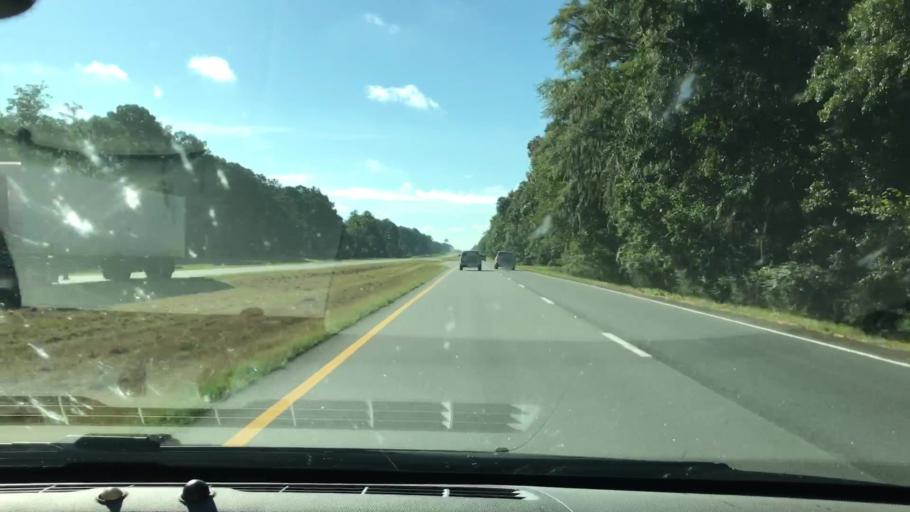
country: US
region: Georgia
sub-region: Lee County
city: Leesburg
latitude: 31.6569
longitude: -84.2717
